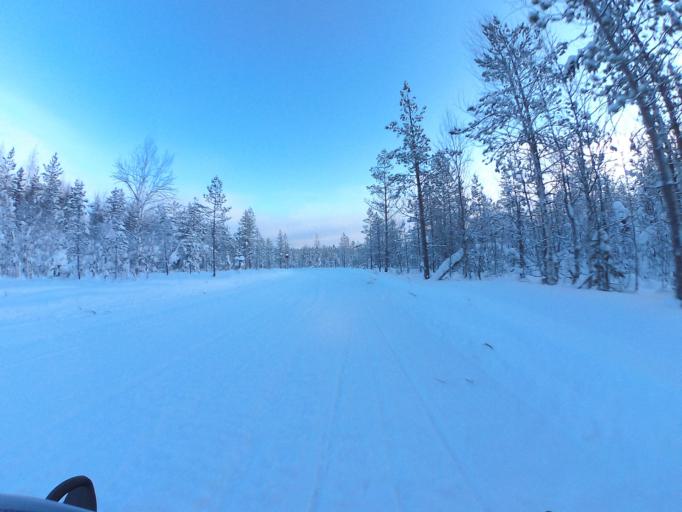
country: FI
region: Lapland
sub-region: Rovaniemi
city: Rovaniemi
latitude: 66.5161
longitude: 26.0017
